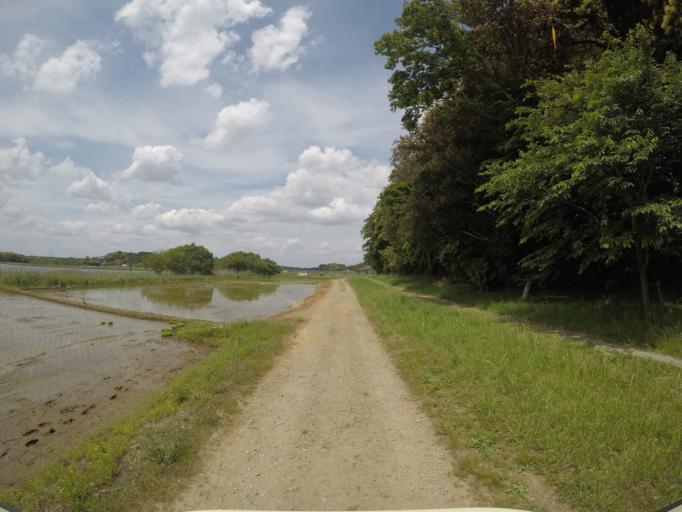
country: JP
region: Ibaraki
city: Ushiku
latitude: 35.9562
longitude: 140.1273
